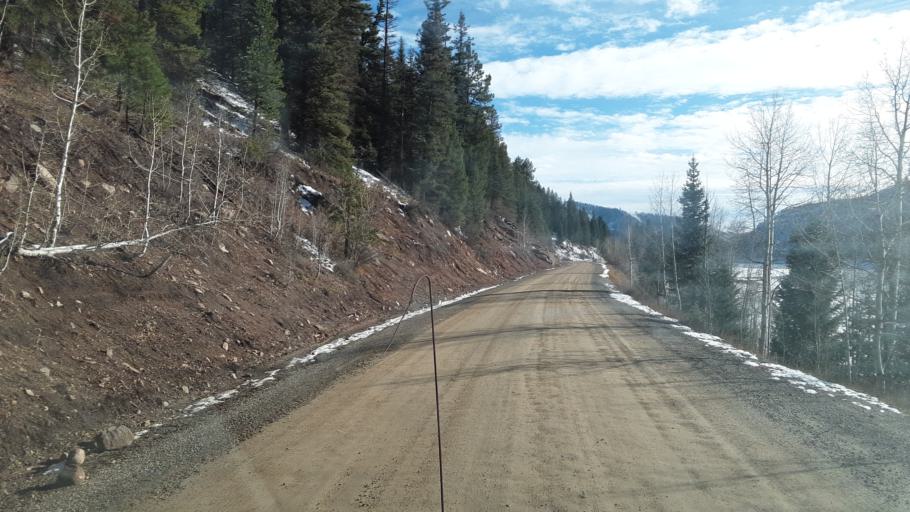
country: US
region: Colorado
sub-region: La Plata County
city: Bayfield
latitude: 37.4166
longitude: -107.6643
